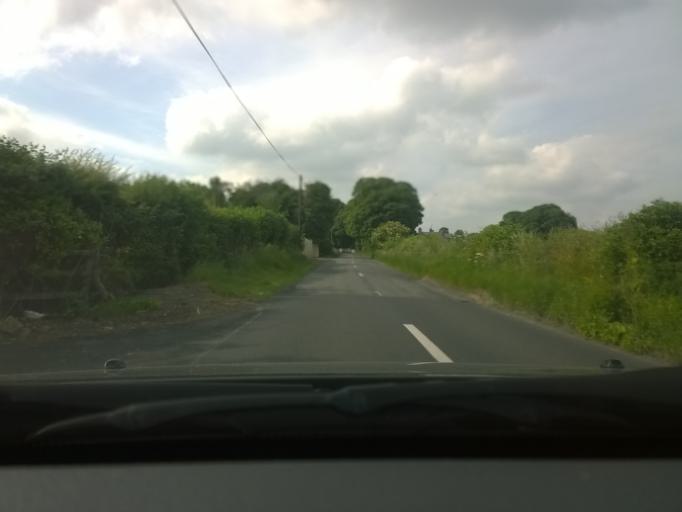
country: IE
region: Leinster
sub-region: Kildare
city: Kildare
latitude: 53.1728
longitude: -6.9136
